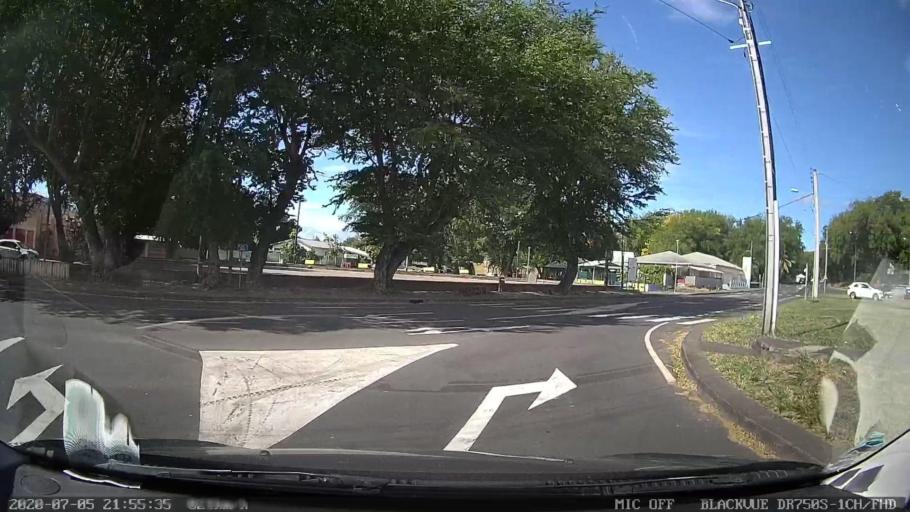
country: RE
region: Reunion
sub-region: Reunion
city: Saint-Denis
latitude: -20.8881
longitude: 55.4863
